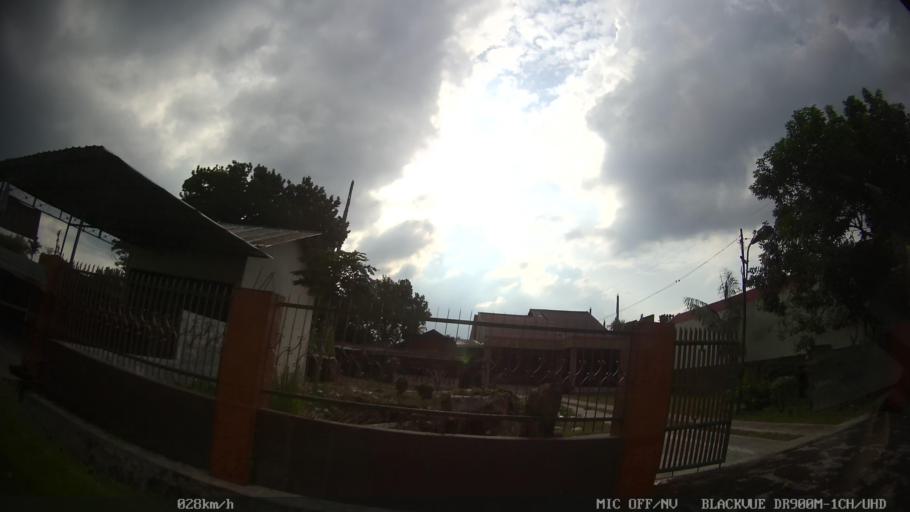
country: ID
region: North Sumatra
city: Sunggal
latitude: 3.5317
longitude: 98.6052
